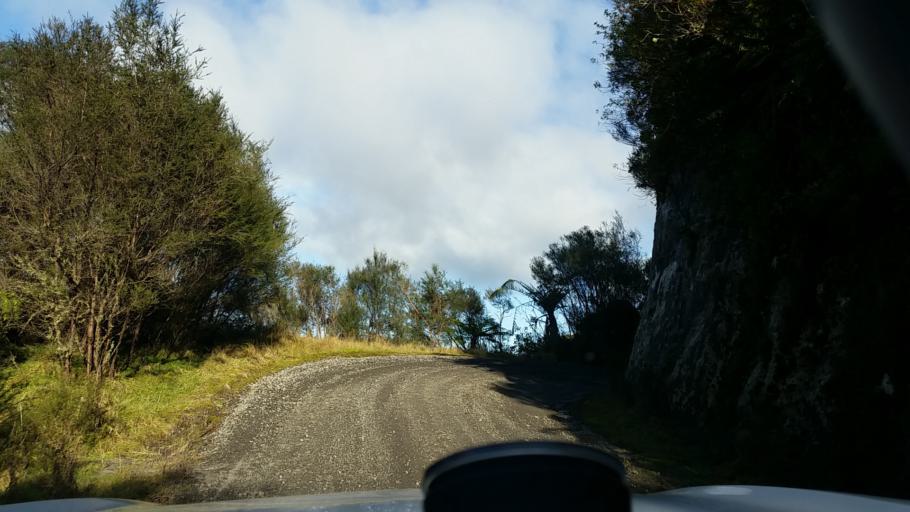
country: NZ
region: Taranaki
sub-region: South Taranaki District
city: Eltham
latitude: -39.4064
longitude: 174.5571
